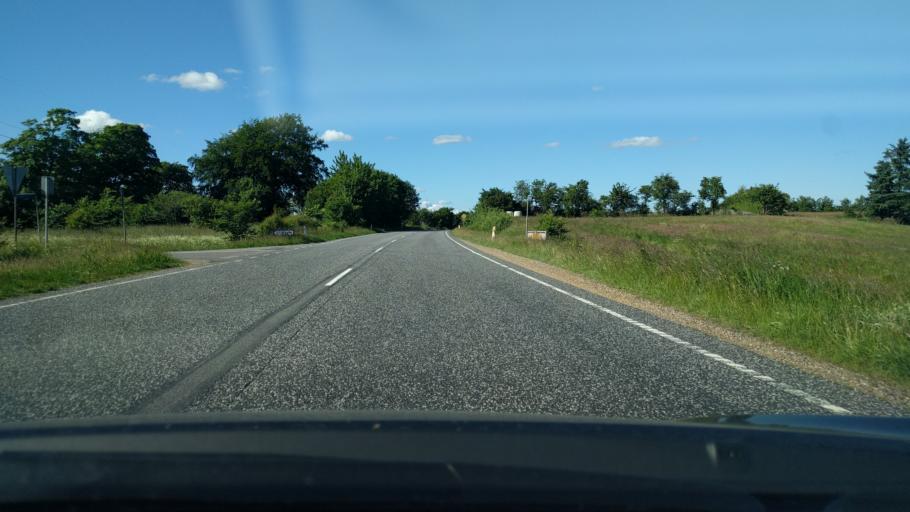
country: DK
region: North Denmark
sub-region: Vesthimmerland Kommune
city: Alestrup
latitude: 56.6701
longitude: 9.5223
